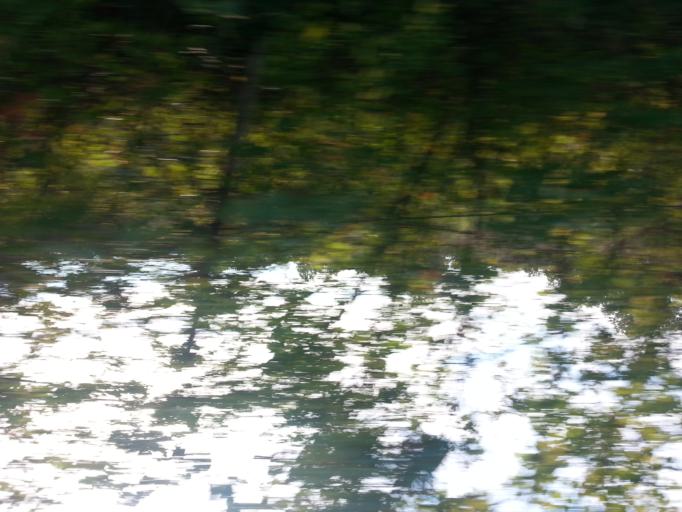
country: US
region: Tennessee
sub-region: Blount County
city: Eagleton Village
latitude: 35.8209
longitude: -83.9362
